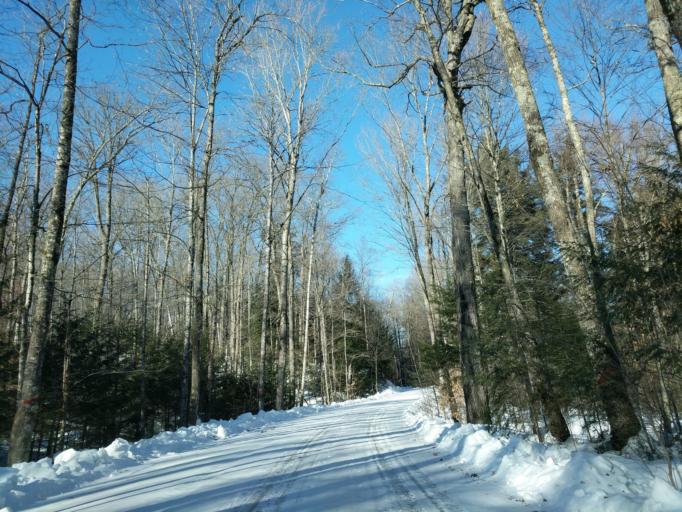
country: US
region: Wisconsin
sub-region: Menominee County
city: Legend Lake
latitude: 45.0936
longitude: -88.5695
